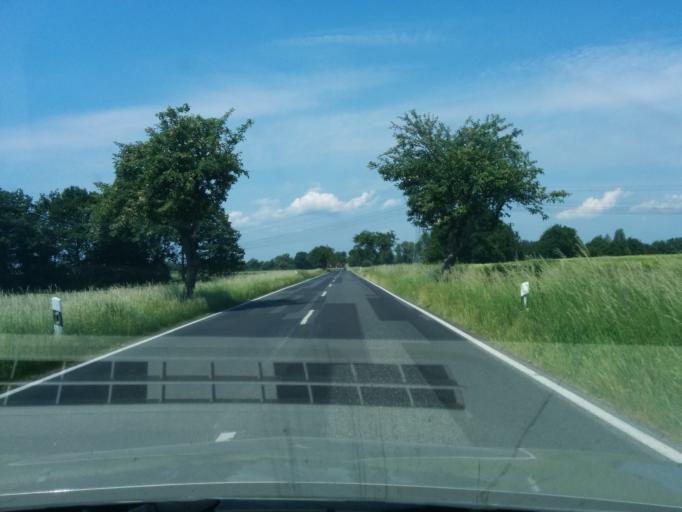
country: DE
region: Brandenburg
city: Ahrensfelde
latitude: 52.6200
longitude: 13.5829
